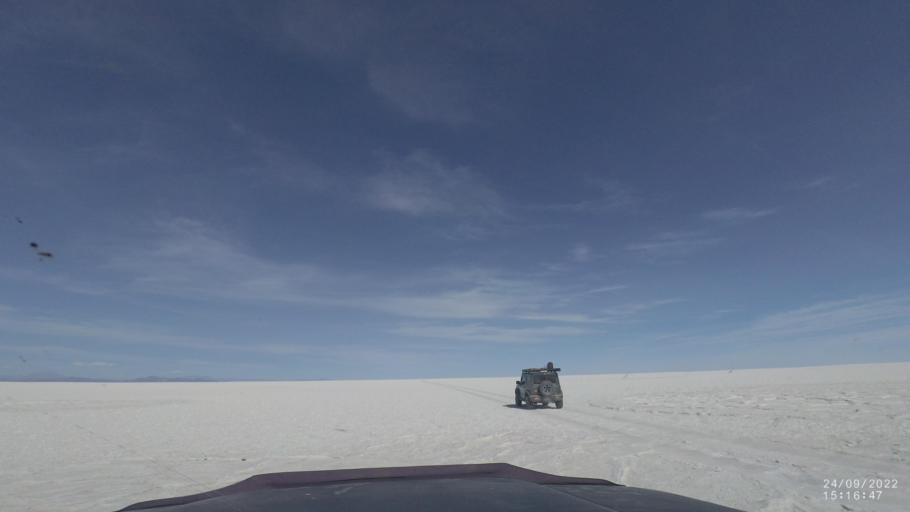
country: BO
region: Potosi
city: Colchani
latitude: -19.9843
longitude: -67.4329
